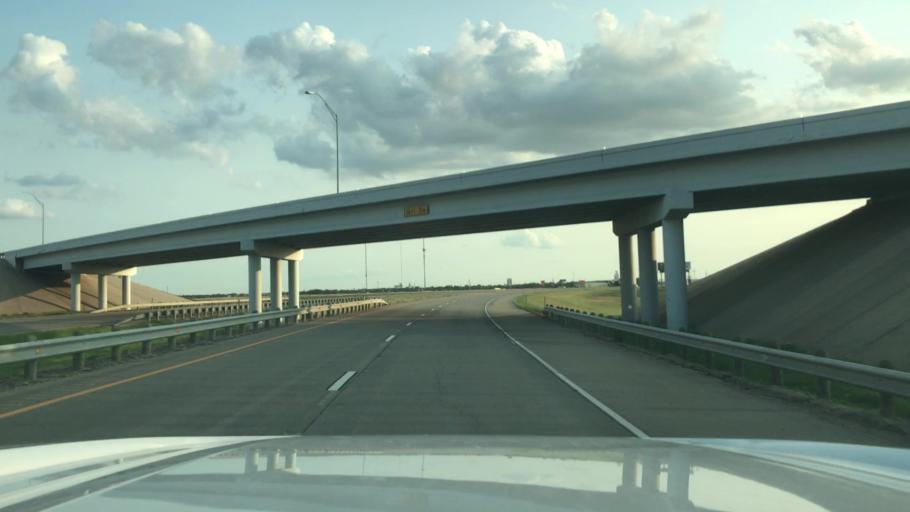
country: US
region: Texas
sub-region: Hale County
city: Seth Ward
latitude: 34.2341
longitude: -101.7098
